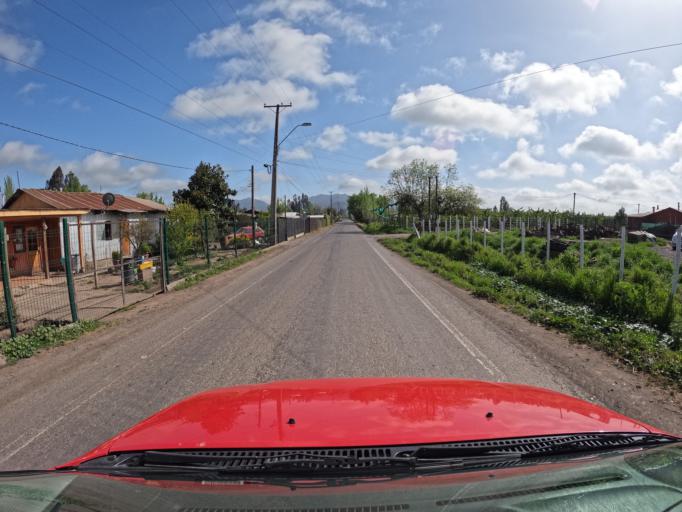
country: CL
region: Maule
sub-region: Provincia de Curico
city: Teno
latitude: -34.8810
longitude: -71.2259
